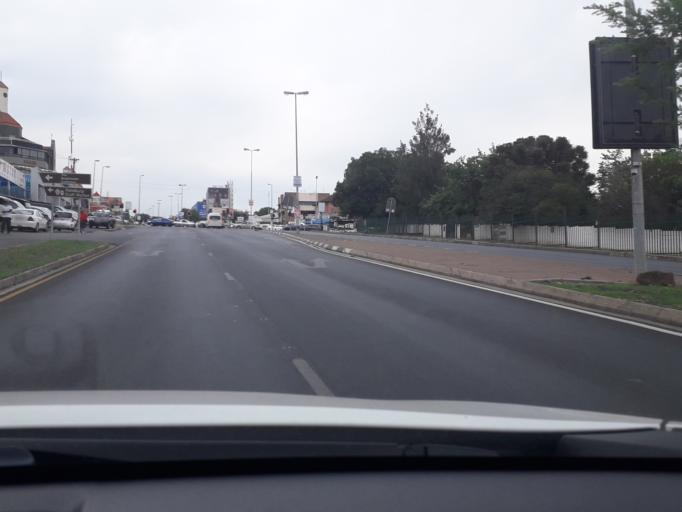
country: ZA
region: Gauteng
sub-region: City of Johannesburg Metropolitan Municipality
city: Johannesburg
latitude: -26.1002
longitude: 28.0113
